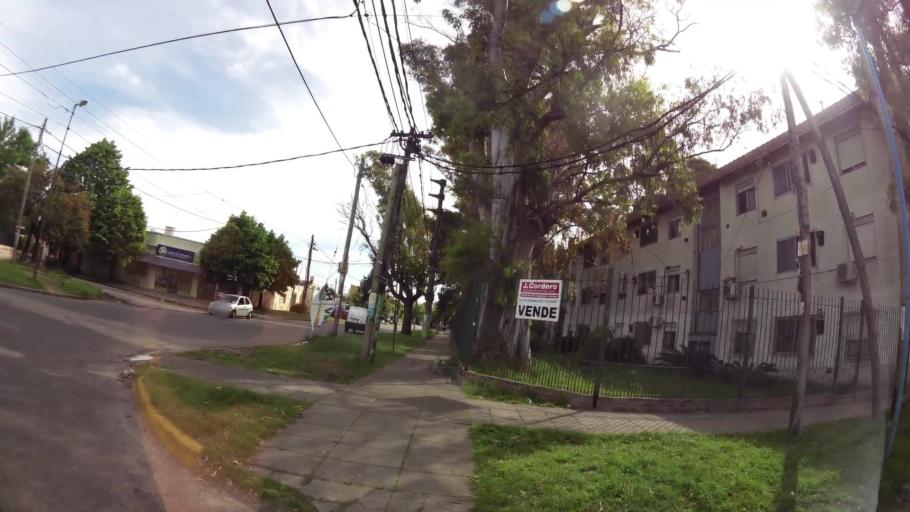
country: AR
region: Buenos Aires
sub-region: Partido de Quilmes
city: Quilmes
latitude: -34.7524
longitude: -58.2800
